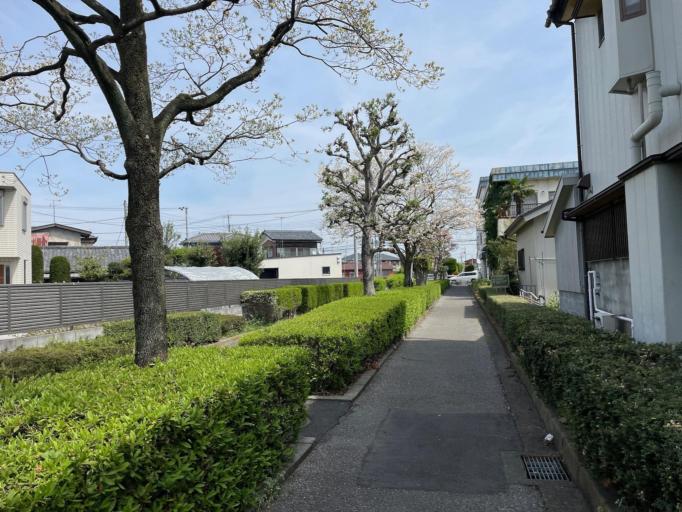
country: JP
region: Saitama
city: Fukayacho
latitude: 36.1914
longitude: 139.2899
